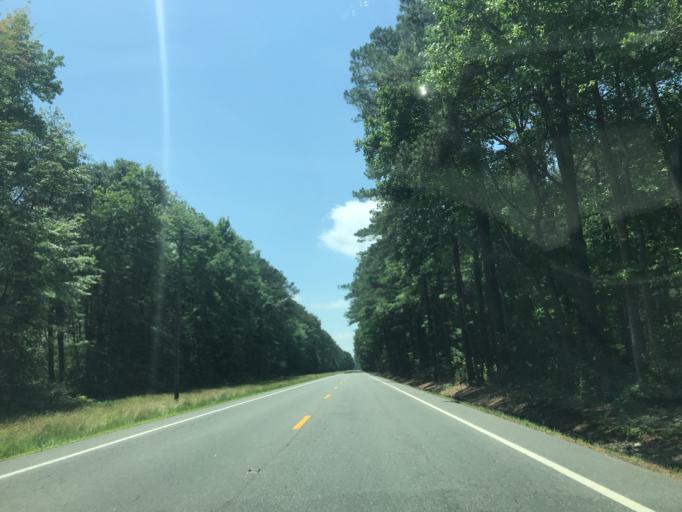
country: US
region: Maryland
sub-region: Caroline County
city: Federalsburg
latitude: 38.6339
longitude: -75.7881
